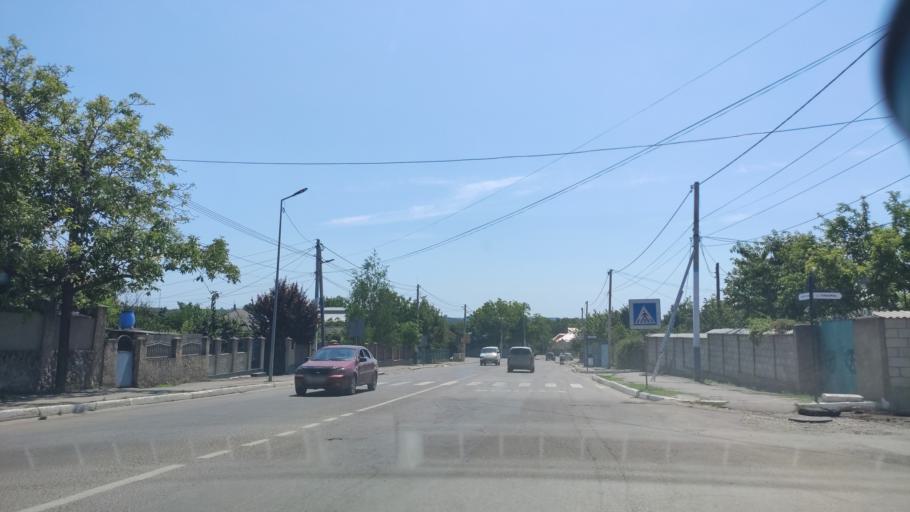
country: MD
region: Raionul Soroca
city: Soroca
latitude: 48.1669
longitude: 28.3034
